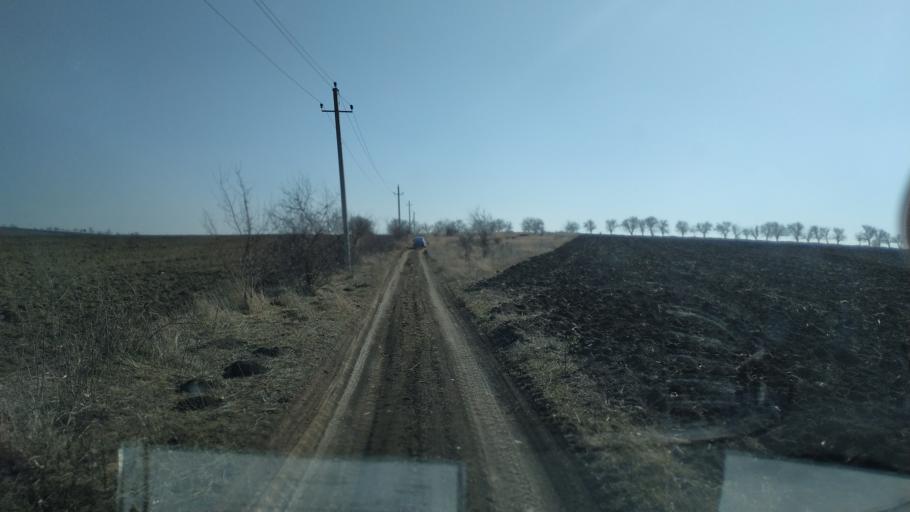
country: MD
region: Causeni
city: Causeni
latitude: 46.5581
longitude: 29.2654
